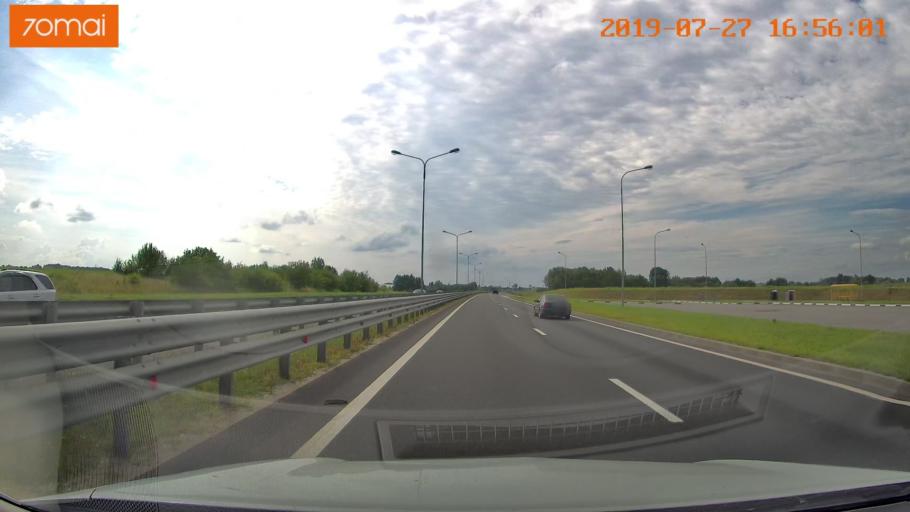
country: RU
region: Kaliningrad
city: Bol'shoe Isakovo
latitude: 54.6929
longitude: 20.7530
